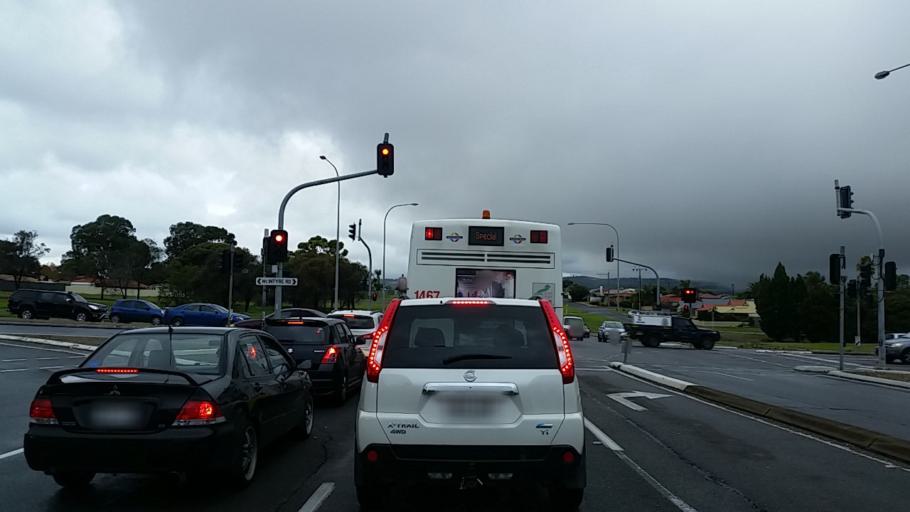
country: AU
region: South Australia
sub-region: Tea Tree Gully
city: Modbury
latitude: -34.8285
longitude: 138.6795
